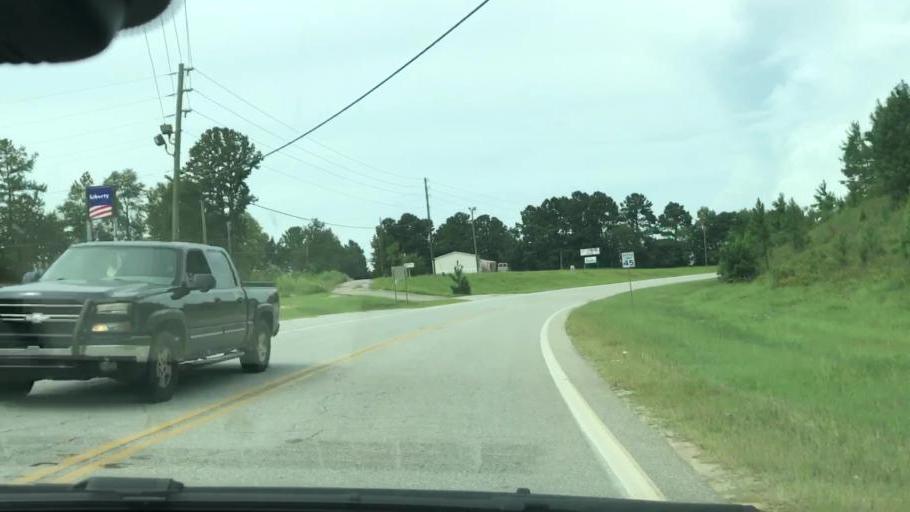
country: US
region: Georgia
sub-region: Clay County
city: Fort Gaines
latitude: 31.6271
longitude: -85.0468
